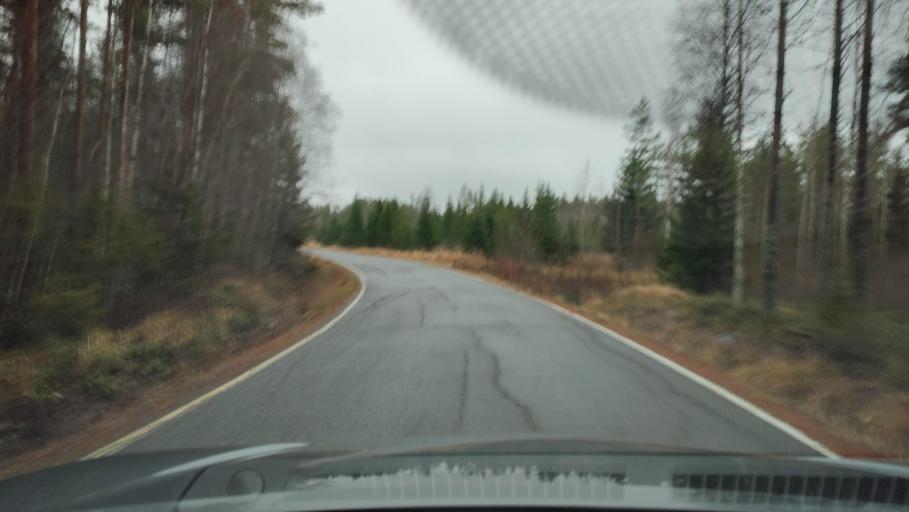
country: FI
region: Southern Ostrobothnia
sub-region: Suupohja
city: Isojoki
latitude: 62.1604
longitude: 21.8868
